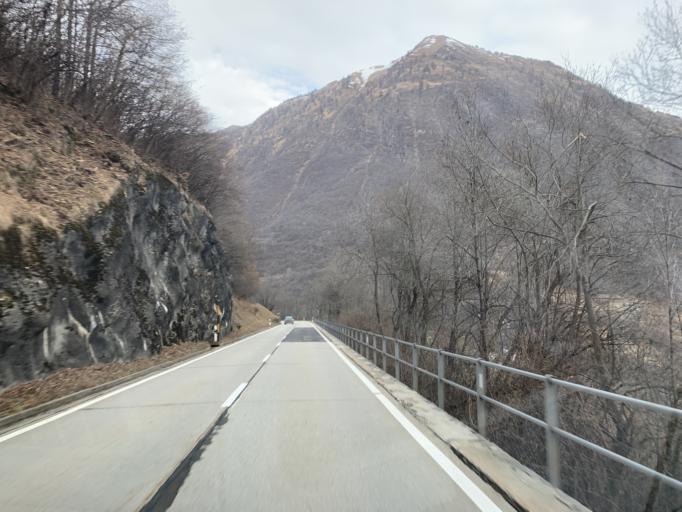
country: CH
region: Ticino
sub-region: Blenio District
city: Cancori
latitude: 46.5227
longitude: 8.9321
